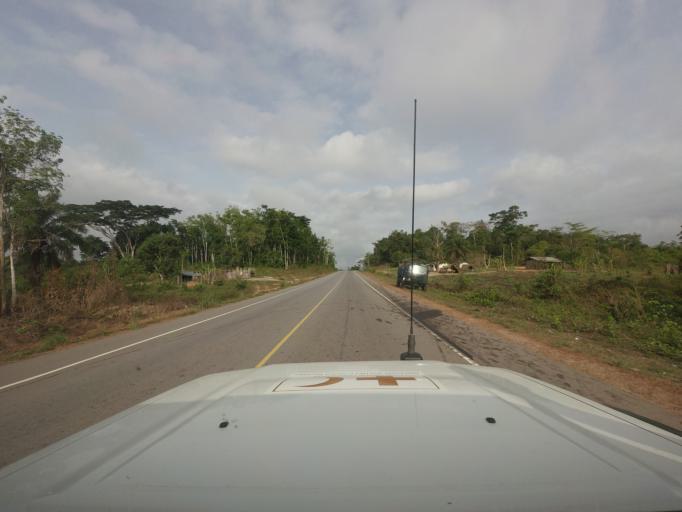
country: LR
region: Bong
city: Gbarnga
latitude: 7.0036
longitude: -9.2966
